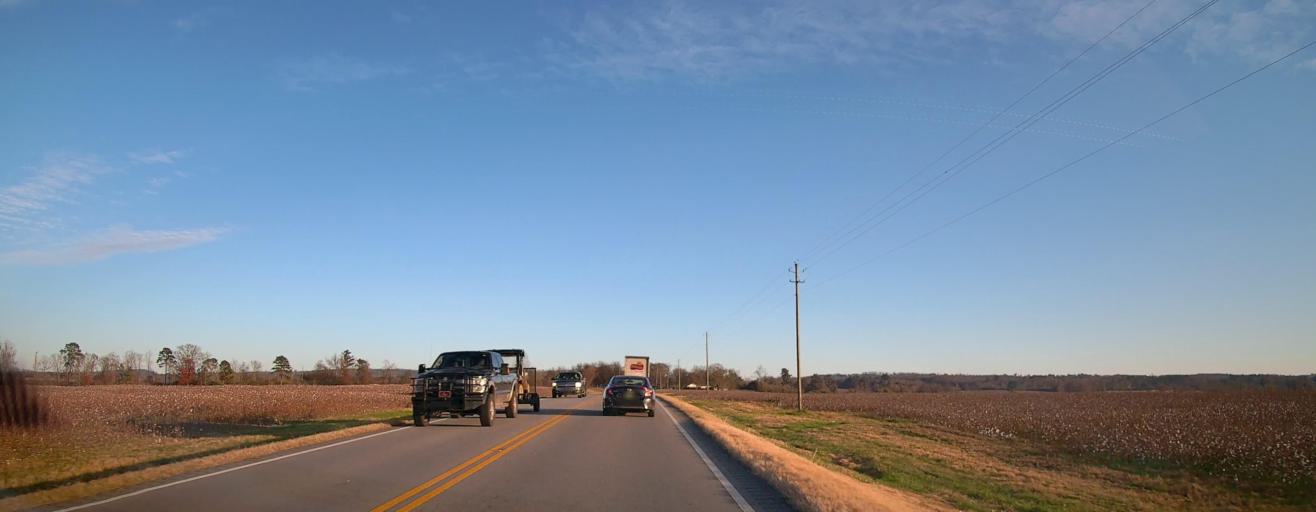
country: US
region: Alabama
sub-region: Blount County
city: Oneonta
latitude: 34.0992
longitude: -86.3634
